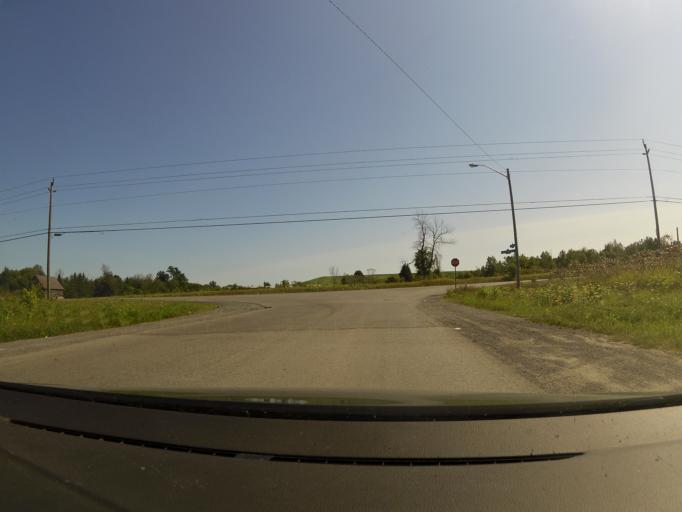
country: CA
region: Ontario
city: Bells Corners
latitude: 45.2912
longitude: -75.9760
